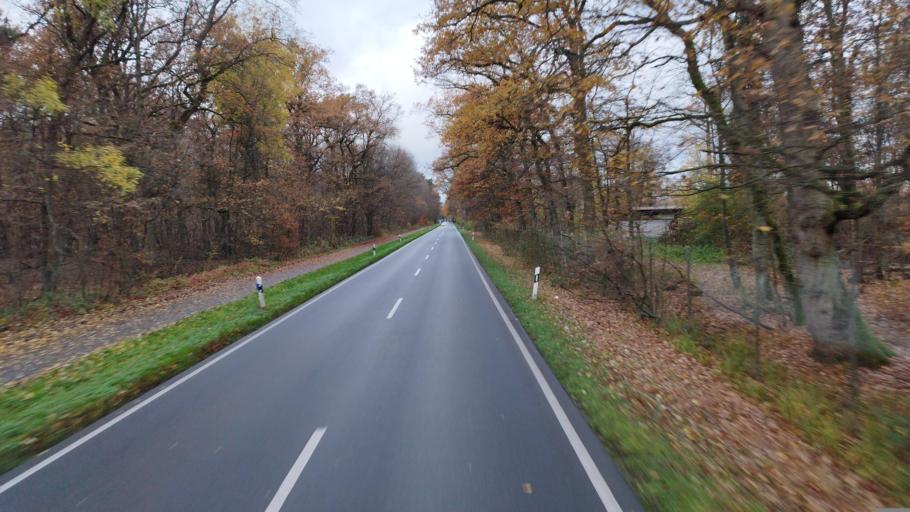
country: DE
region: Rheinland-Pfalz
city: Hatzenbuhl
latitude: 49.1327
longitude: 8.2208
